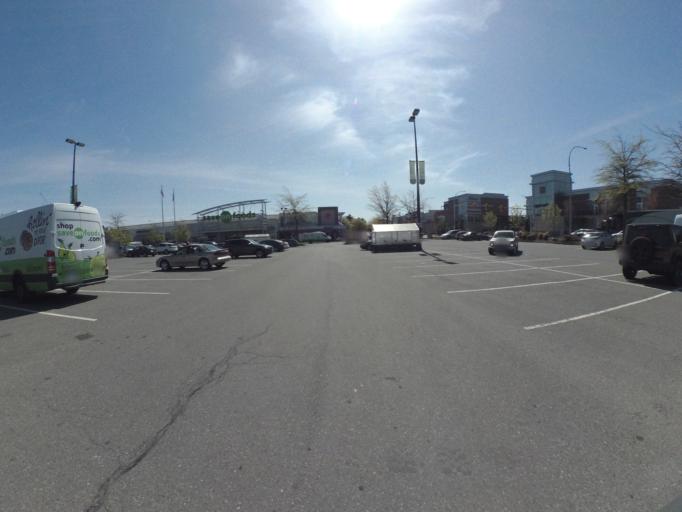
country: CA
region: British Columbia
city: Victoria
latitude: 48.4569
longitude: -123.3748
